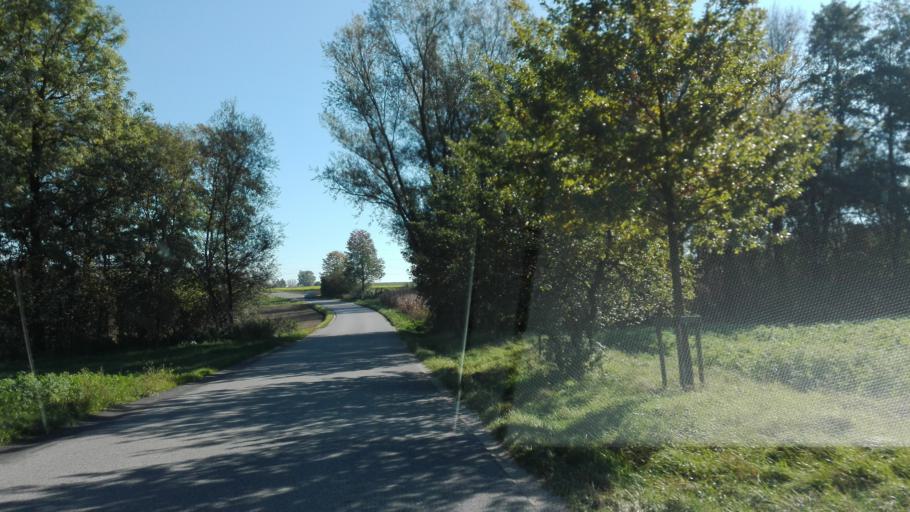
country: AT
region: Upper Austria
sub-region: Politischer Bezirk Linz-Land
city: Pasching
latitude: 48.2834
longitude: 14.1851
